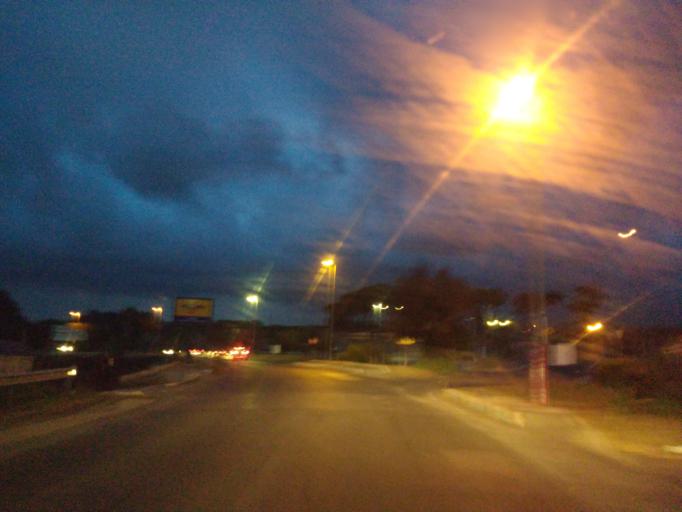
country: IT
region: Latium
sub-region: Citta metropolitana di Roma Capitale
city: Anzio
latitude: 41.4539
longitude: 12.6226
